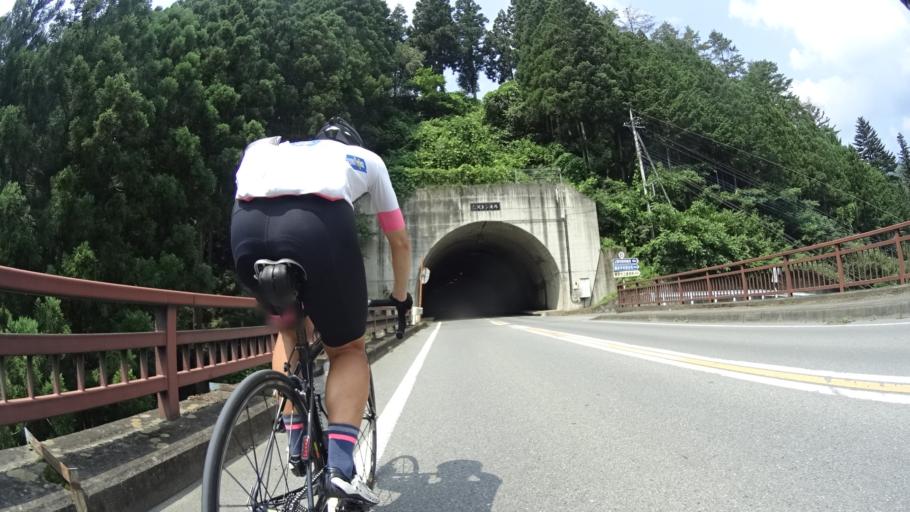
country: JP
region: Gunma
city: Tomioka
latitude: 36.0832
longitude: 138.7597
